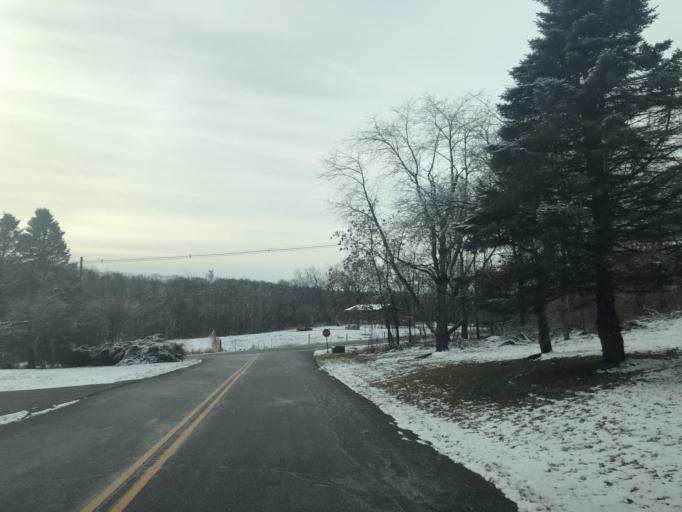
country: US
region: New Jersey
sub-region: Warren County
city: Belvidere
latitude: 40.9315
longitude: -75.0391
